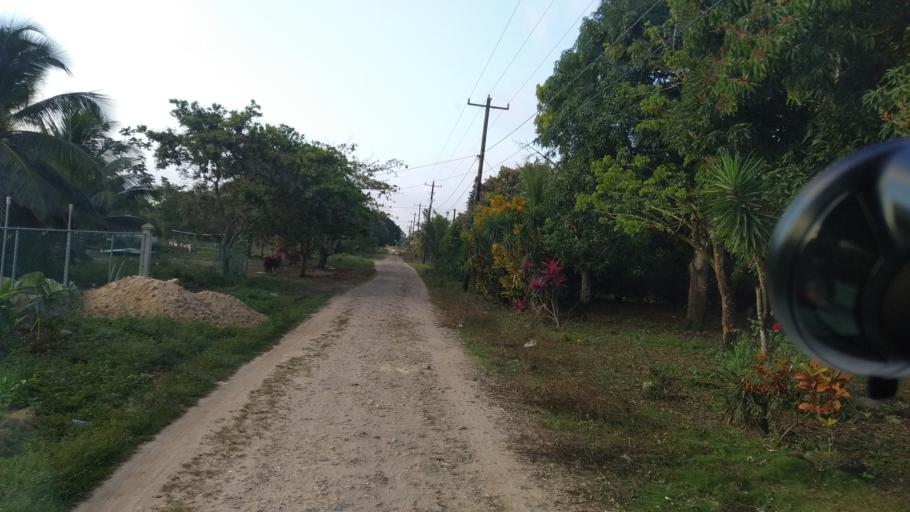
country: BZ
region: Stann Creek
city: Placencia
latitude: 16.5709
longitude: -88.5268
